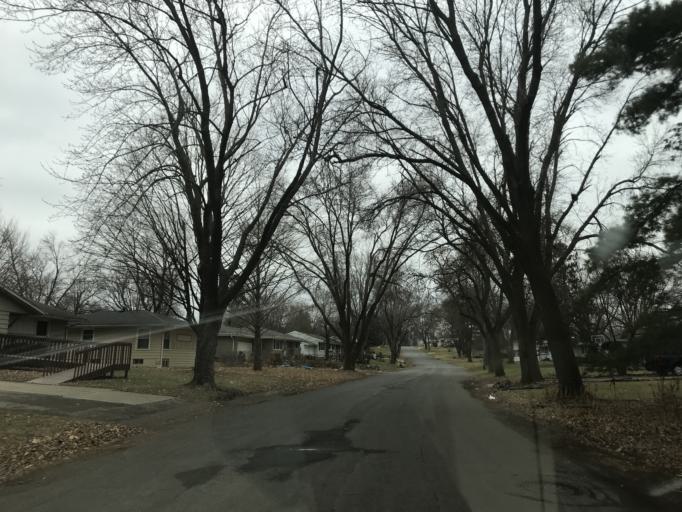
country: US
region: Wisconsin
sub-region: Dane County
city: Monona
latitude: 43.0696
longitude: -89.3130
